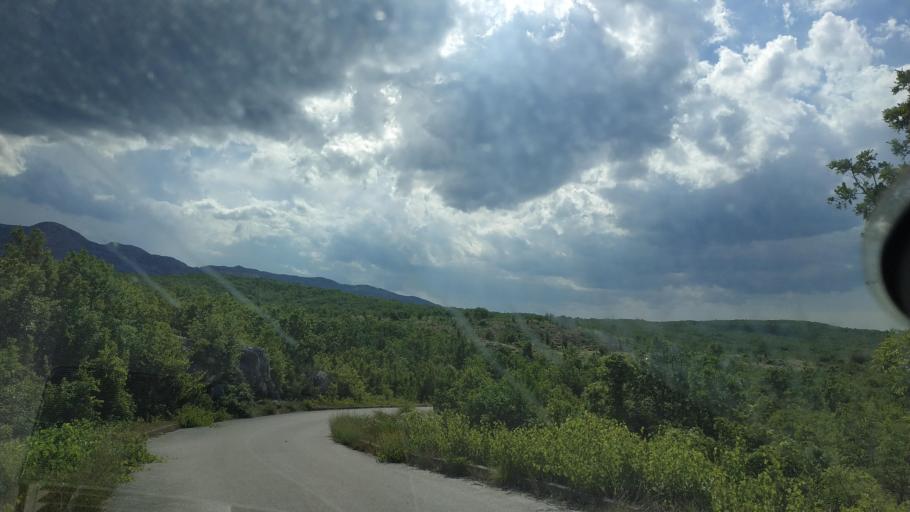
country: HR
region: Splitsko-Dalmatinska
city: Greda
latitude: 43.5800
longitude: 16.6560
